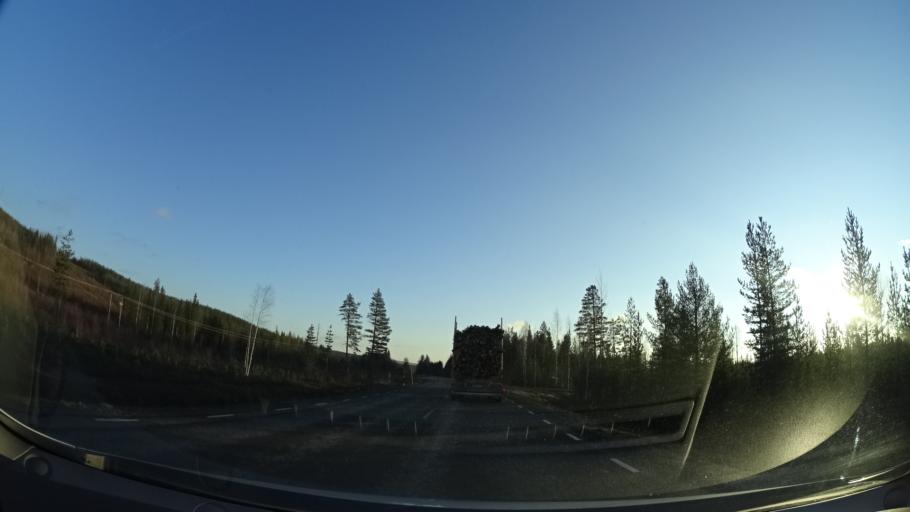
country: SE
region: Vaesterbotten
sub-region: Lycksele Kommun
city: Lycksele
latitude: 64.6475
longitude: 18.6613
